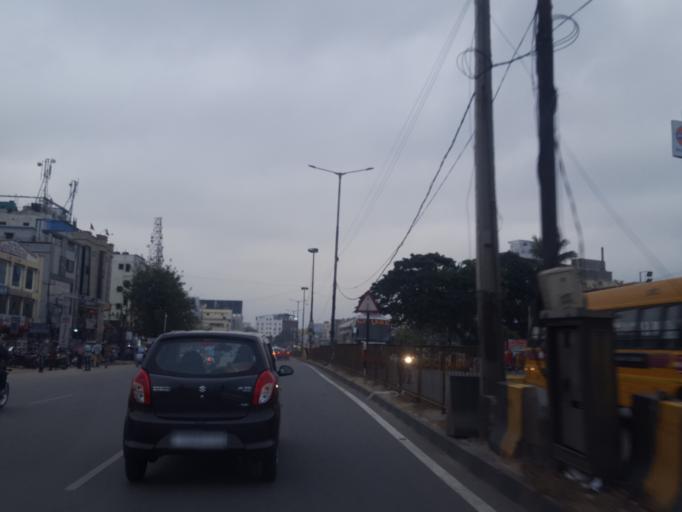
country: IN
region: Telangana
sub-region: Medak
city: Serilingampalle
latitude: 17.5047
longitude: 78.3081
